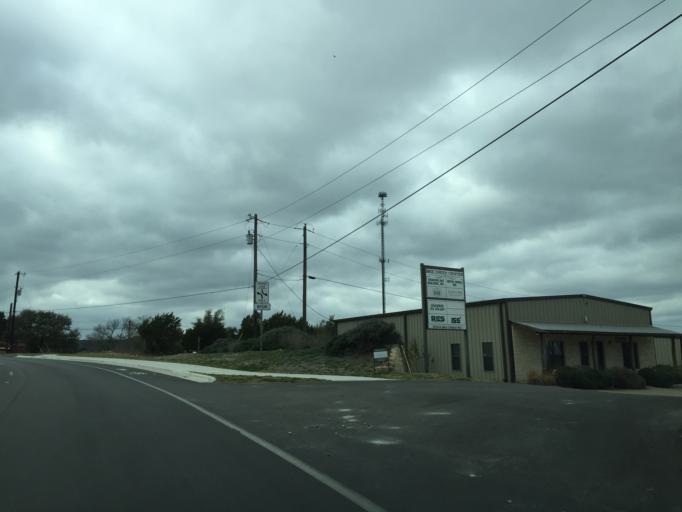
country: US
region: Texas
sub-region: Travis County
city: The Hills
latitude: 30.3352
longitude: -98.0238
